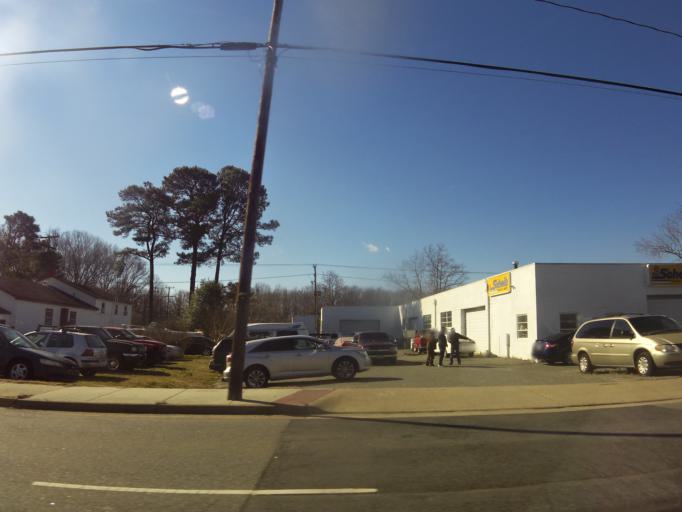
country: US
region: Virginia
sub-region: City of Newport News
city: Newport News
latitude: 37.0030
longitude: -76.4345
